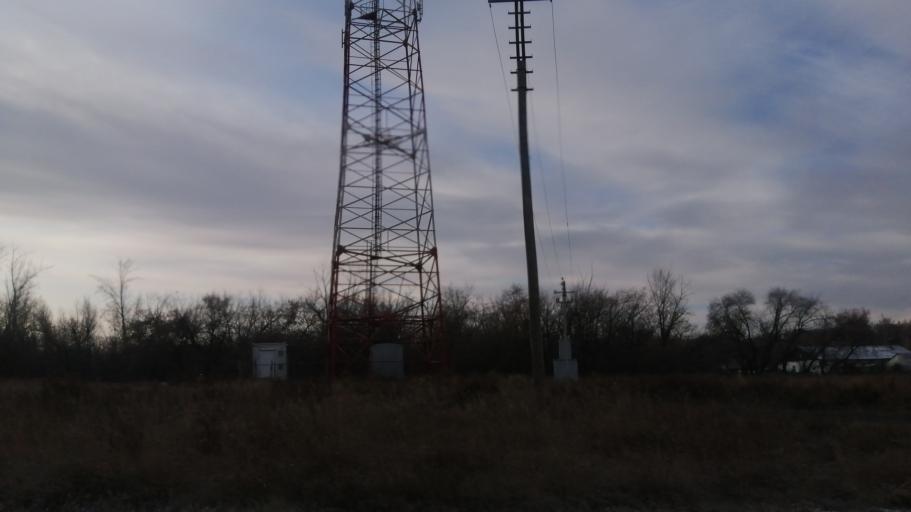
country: RU
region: Novosibirsk
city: Krasnozerskoye
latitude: 53.9887
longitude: 78.7257
